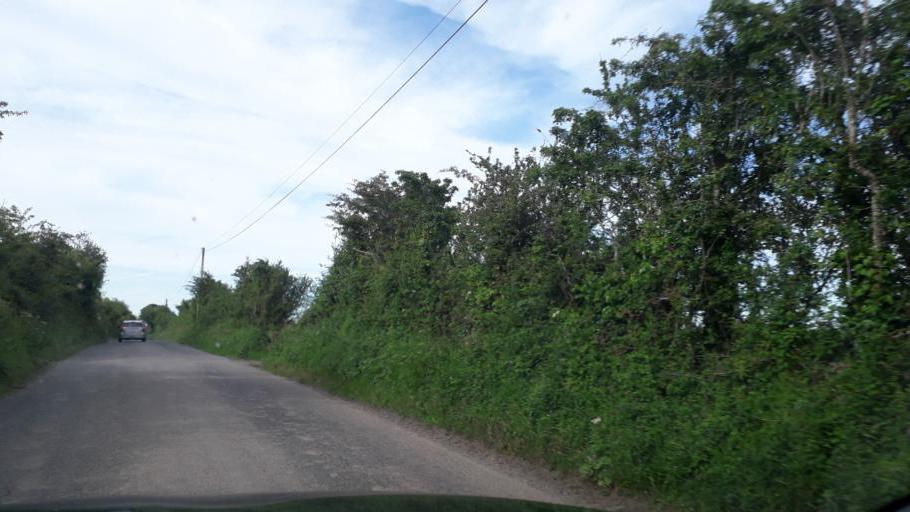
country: IE
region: Leinster
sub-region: Loch Garman
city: Courtown
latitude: 52.5252
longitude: -6.2705
